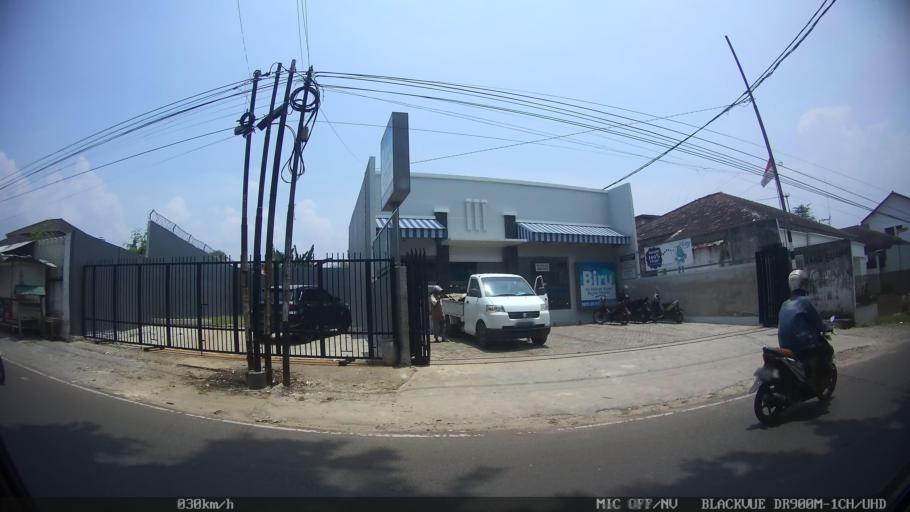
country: ID
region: Lampung
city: Bandarlampung
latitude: -5.4414
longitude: 105.2734
